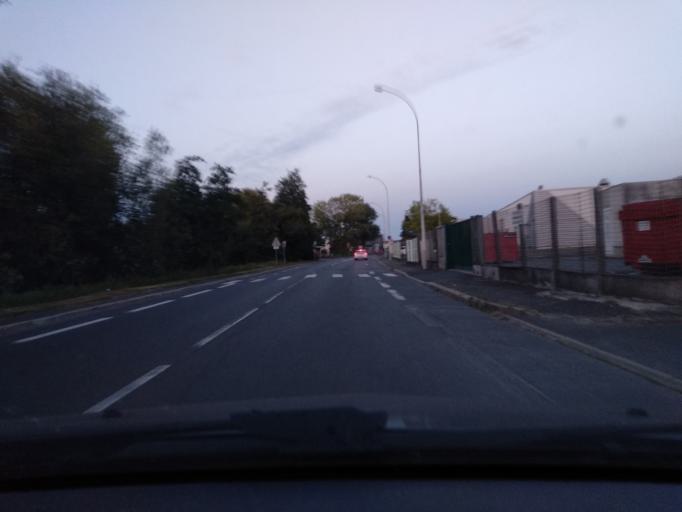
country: FR
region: Centre
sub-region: Departement d'Indre-et-Loire
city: Chanceaux-sur-Choisille
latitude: 47.4352
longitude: 0.6919
